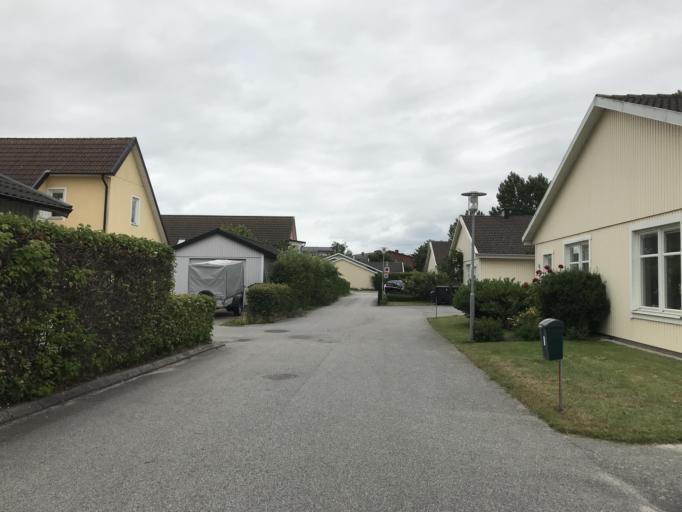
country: SE
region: Skane
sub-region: Burlovs Kommun
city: Arloev
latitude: 55.6351
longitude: 13.0628
